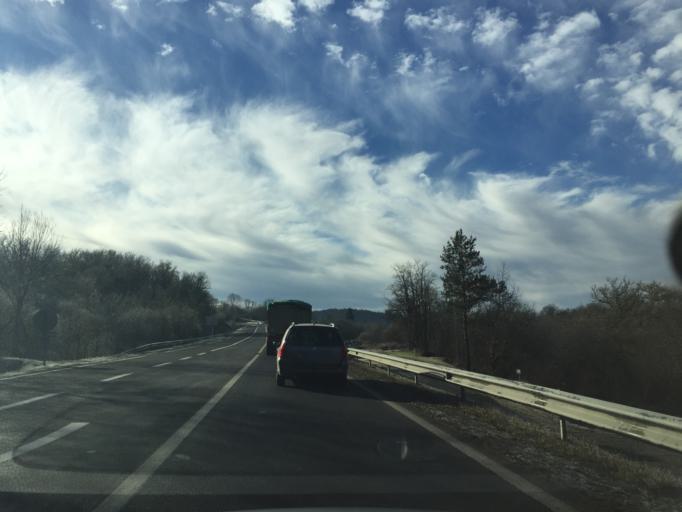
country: FR
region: Auvergne
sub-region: Departement du Puy-de-Dome
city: Gelles
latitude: 45.8600
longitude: 2.6717
